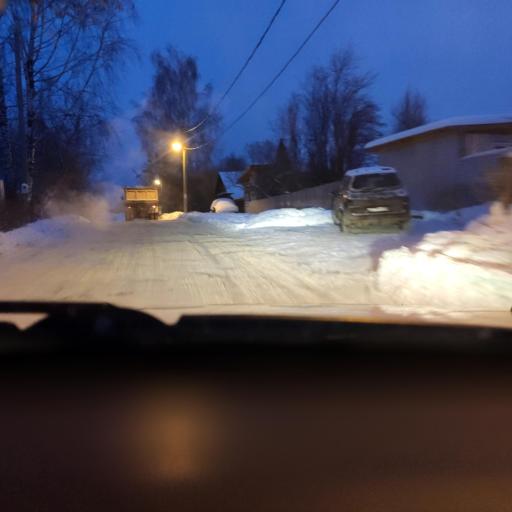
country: RU
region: Perm
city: Perm
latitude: 58.0239
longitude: 56.2803
